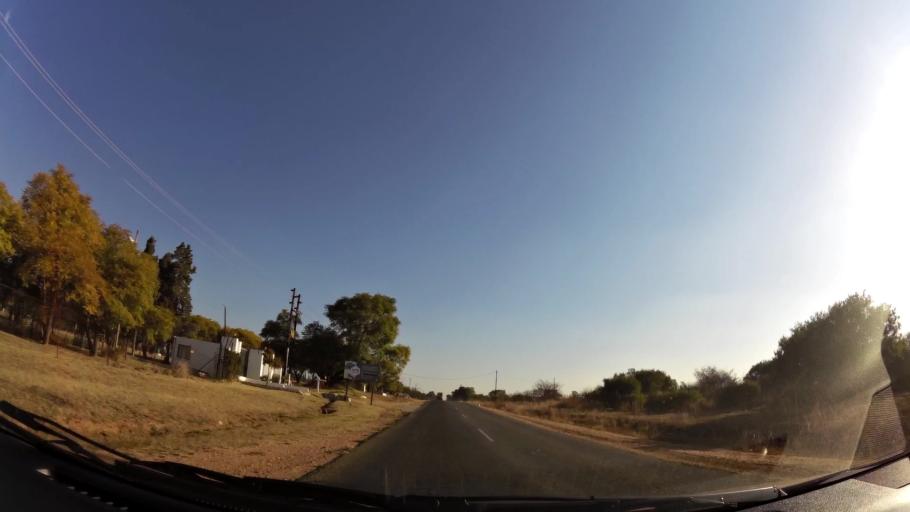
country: ZA
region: Gauteng
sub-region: West Rand District Municipality
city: Muldersdriseloop
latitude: -26.0135
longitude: 27.8901
